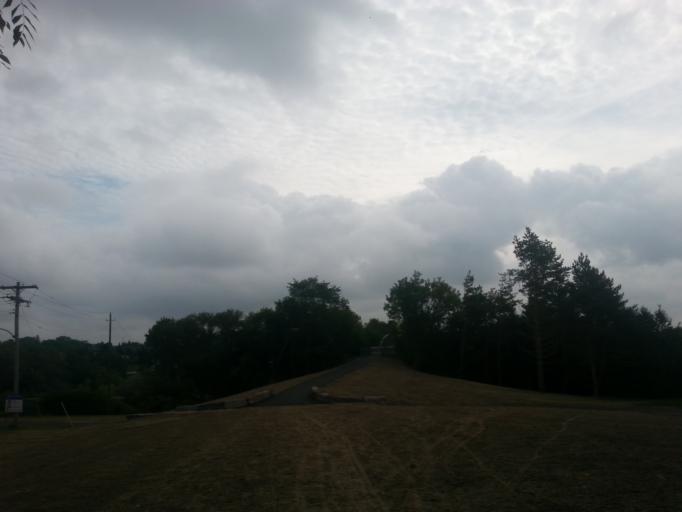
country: CA
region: Ontario
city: Omemee
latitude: 44.3518
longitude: -78.7258
